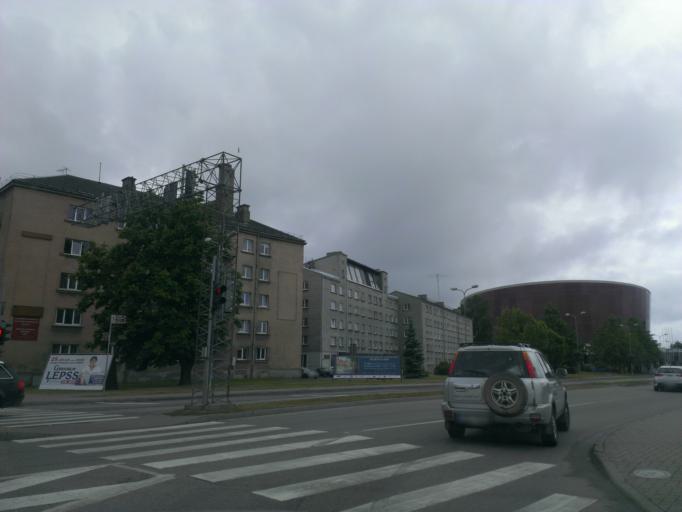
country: LV
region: Liepaja
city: Liepaja
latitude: 56.5121
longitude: 21.0142
